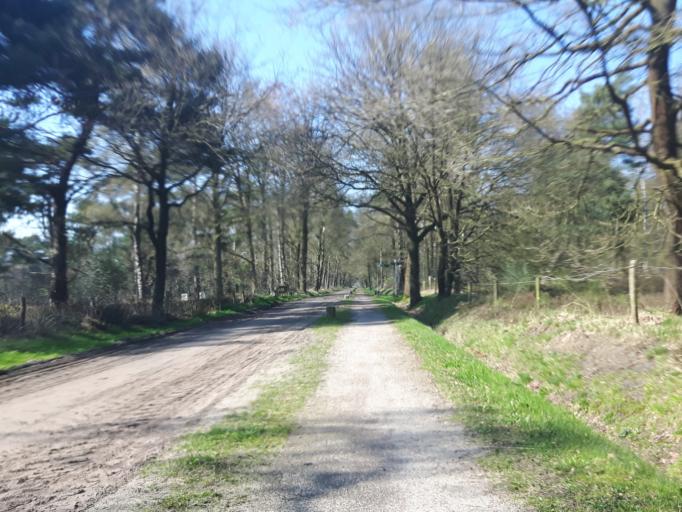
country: NL
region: Overijssel
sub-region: Gemeente Haaksbergen
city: Haaksbergen
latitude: 52.1805
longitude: 6.8185
